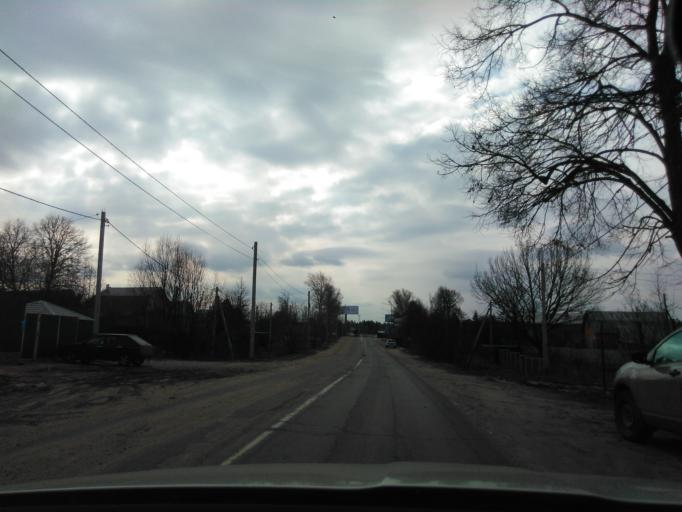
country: RU
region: Moskovskaya
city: Marfino
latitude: 56.0465
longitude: 37.5374
